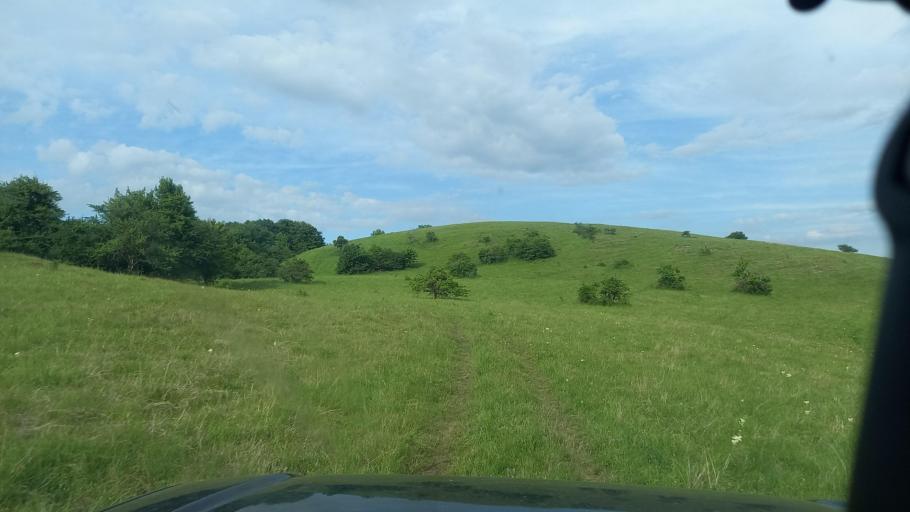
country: RU
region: Karachayevo-Cherkesiya
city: Kurdzhinovo
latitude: 44.1272
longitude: 41.0621
